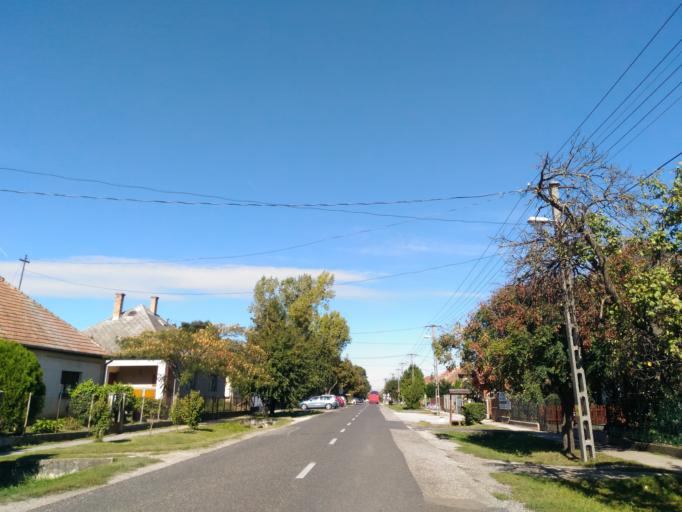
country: HU
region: Fejer
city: Ivancsa
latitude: 47.1492
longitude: 18.8290
